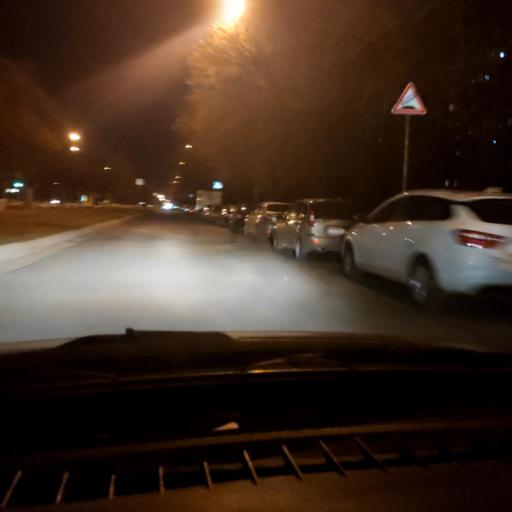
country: RU
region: Samara
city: Tol'yatti
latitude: 53.5192
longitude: 49.2920
